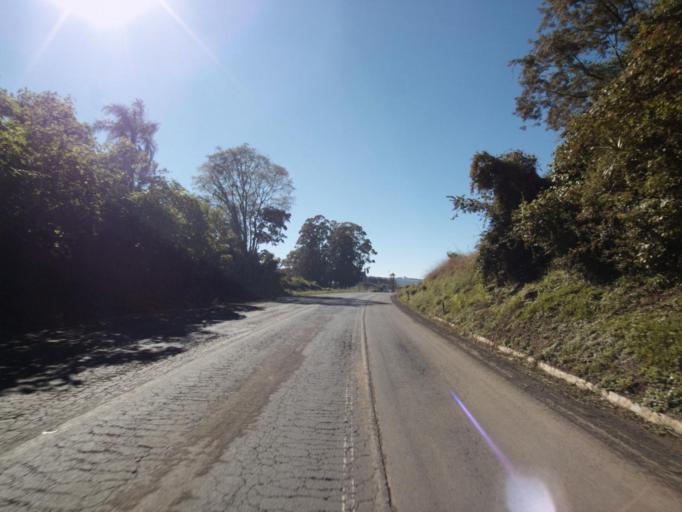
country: BR
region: Rio Grande do Sul
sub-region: Frederico Westphalen
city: Frederico Westphalen
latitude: -26.9196
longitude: -53.1970
